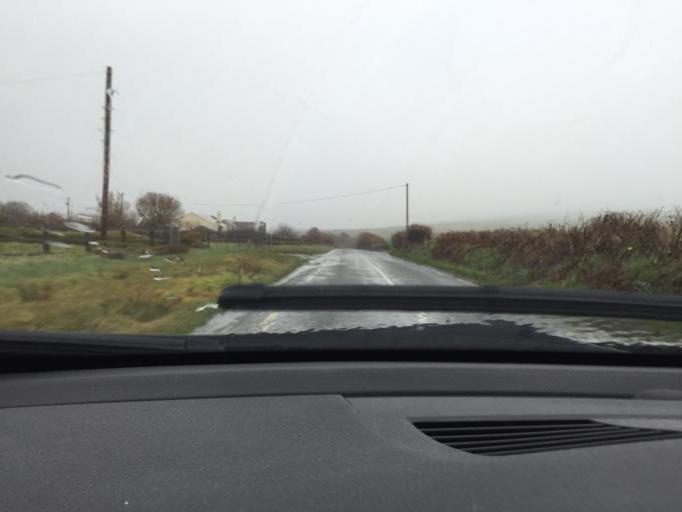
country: IE
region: Munster
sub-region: Ciarrai
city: Dingle
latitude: 52.1235
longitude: -10.3308
